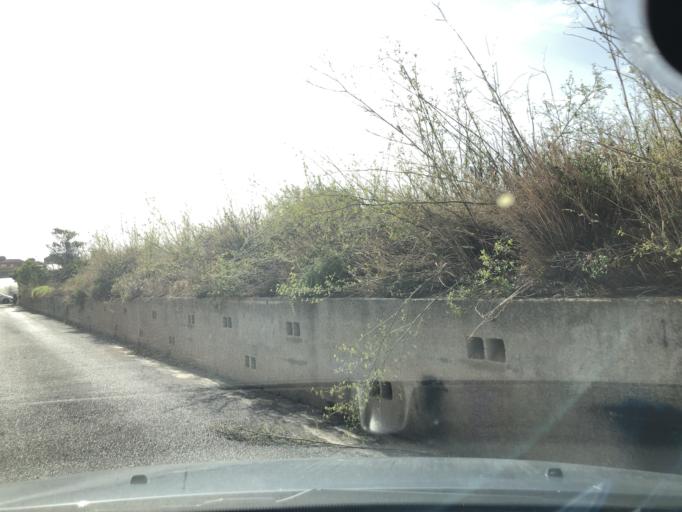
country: ES
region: Valencia
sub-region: Provincia de Alicante
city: Callosa d'En Sarria
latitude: 38.6494
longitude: -0.1253
